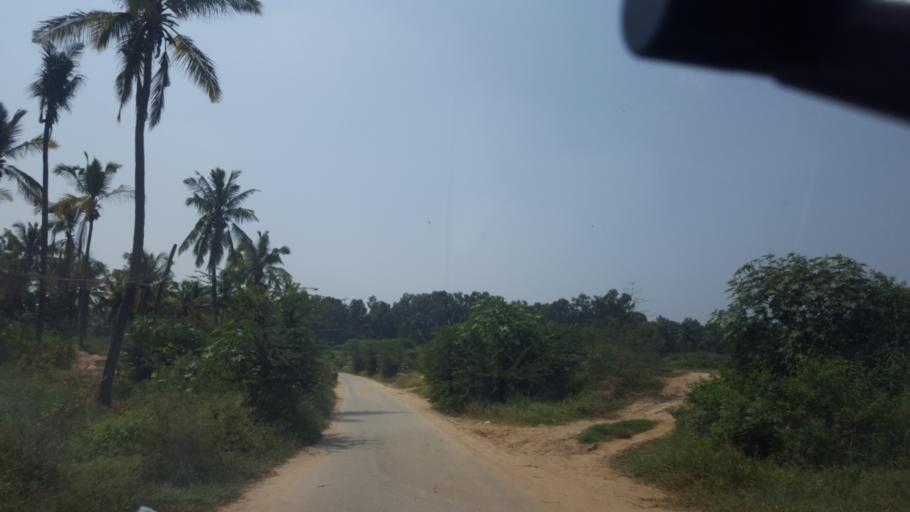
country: IN
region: Karnataka
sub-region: Bangalore Urban
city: Bangalore
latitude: 12.9385
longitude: 77.7099
